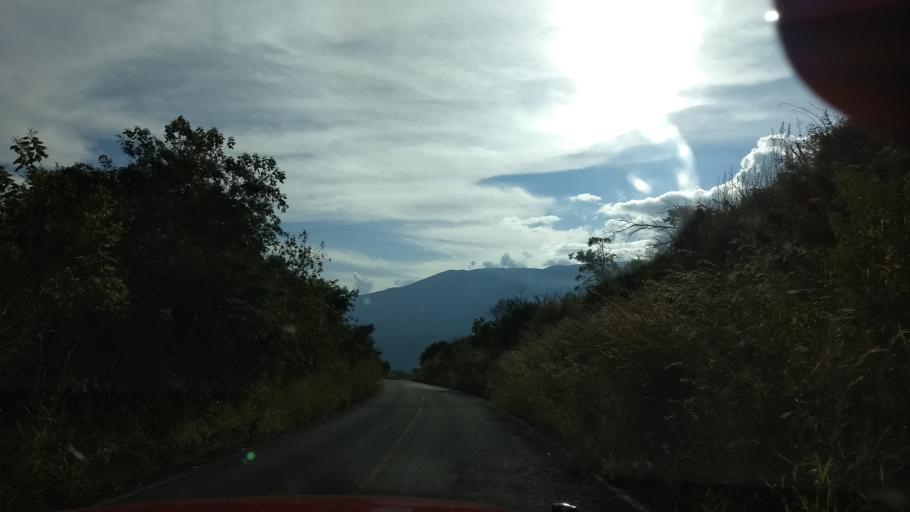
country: MX
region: Colima
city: Suchitlan
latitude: 19.4642
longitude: -103.7846
